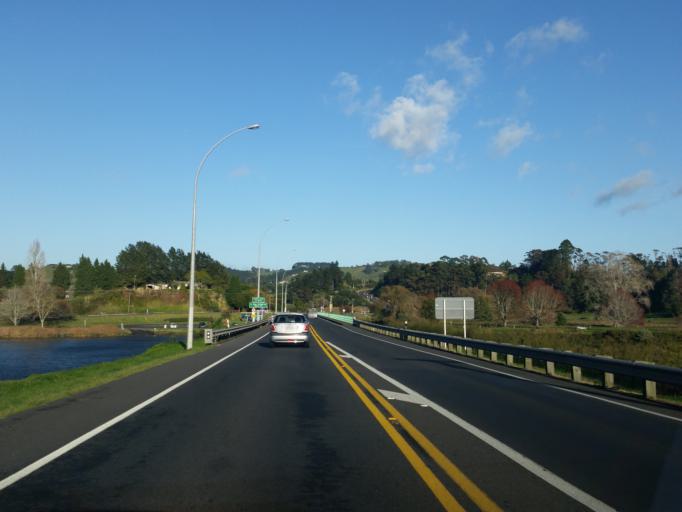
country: NZ
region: Bay of Plenty
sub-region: Tauranga City
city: Tauranga
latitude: -37.6980
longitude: 176.0963
